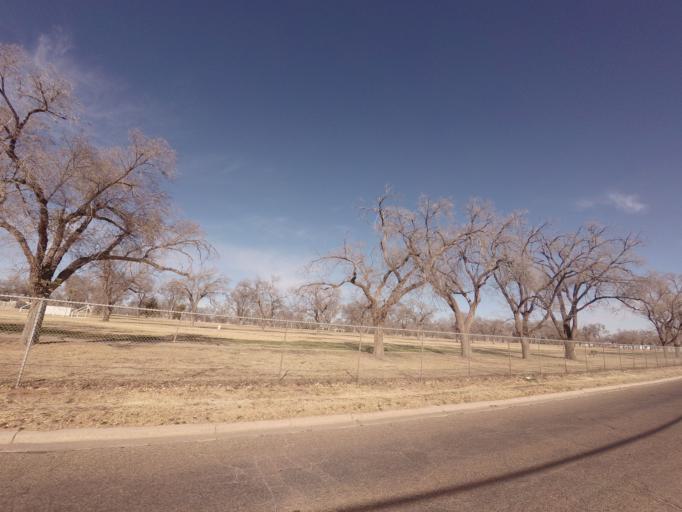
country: US
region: New Mexico
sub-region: Curry County
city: Clovis
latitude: 34.4048
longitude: -103.1835
